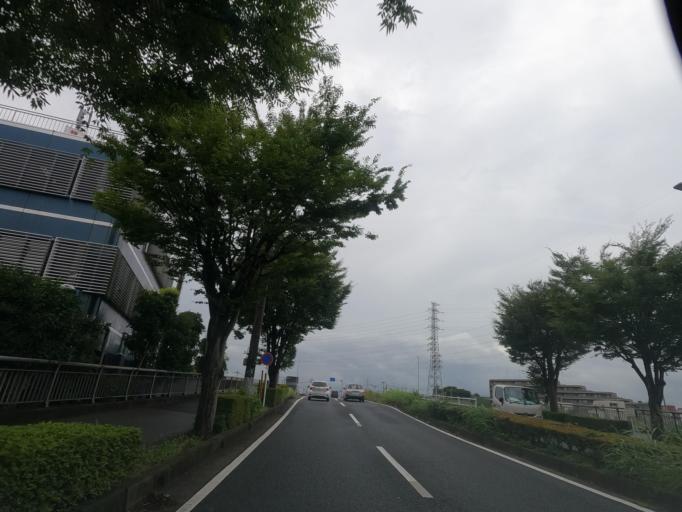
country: JP
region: Saitama
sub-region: Kawaguchi-shi
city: Hatogaya-honcho
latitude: 35.8503
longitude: 139.7089
